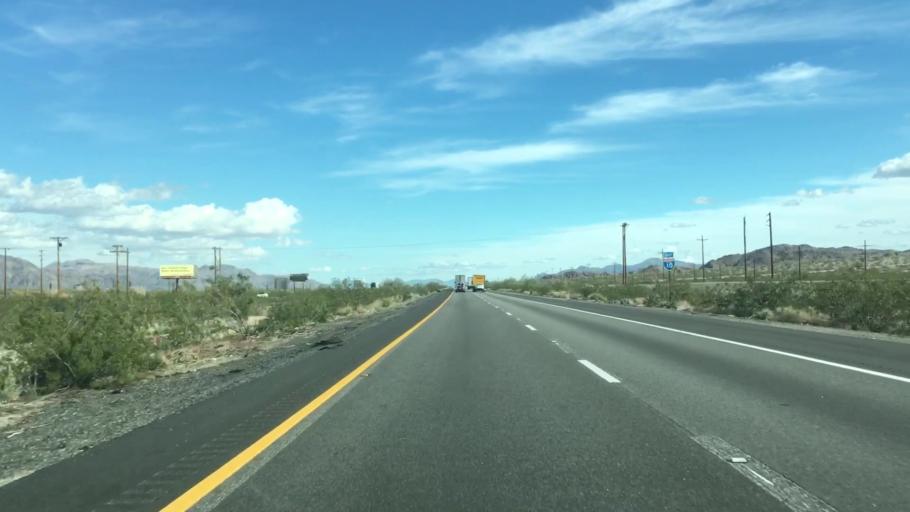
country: US
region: California
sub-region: Riverside County
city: Mecca
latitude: 33.6609
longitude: -115.7164
